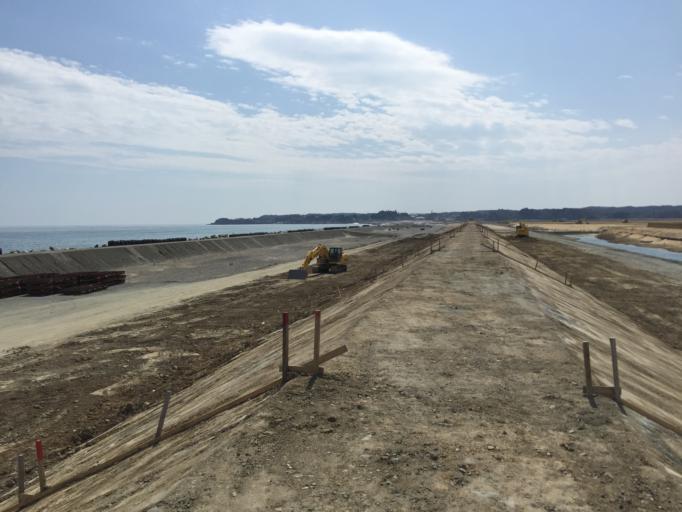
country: JP
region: Miyagi
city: Marumori
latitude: 37.7823
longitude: 140.9870
